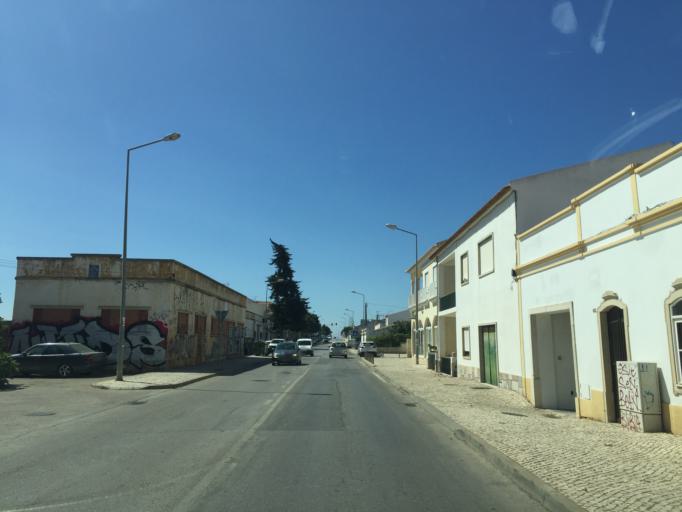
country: PT
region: Faro
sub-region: Albufeira
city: Ferreiras
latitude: 37.1267
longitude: -8.2441
